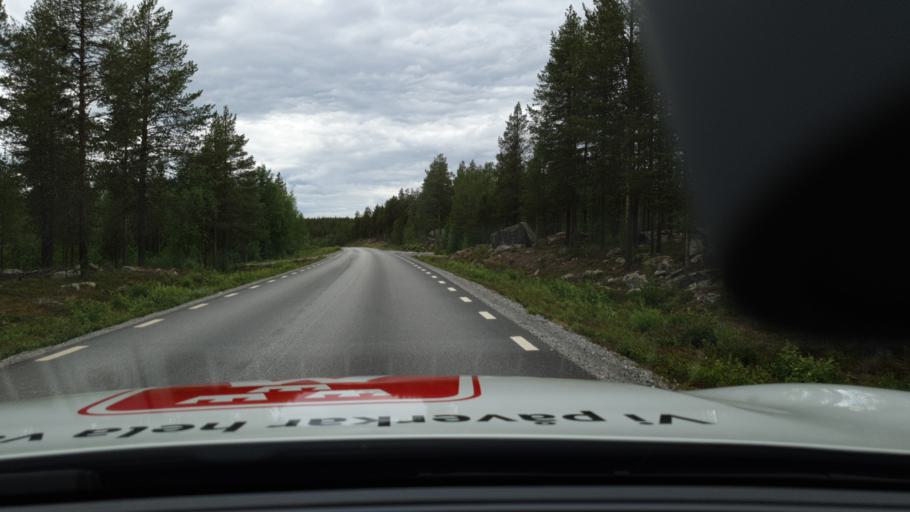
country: SE
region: Norrbotten
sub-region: Jokkmokks Kommun
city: Jokkmokk
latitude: 66.8531
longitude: 18.9596
